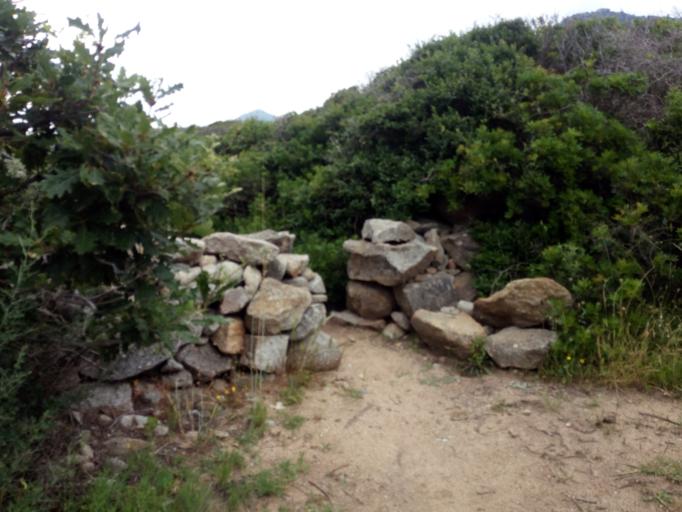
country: FR
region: Corsica
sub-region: Departement de la Haute-Corse
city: L'Ile-Rousse
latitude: 42.6279
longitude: 8.8982
